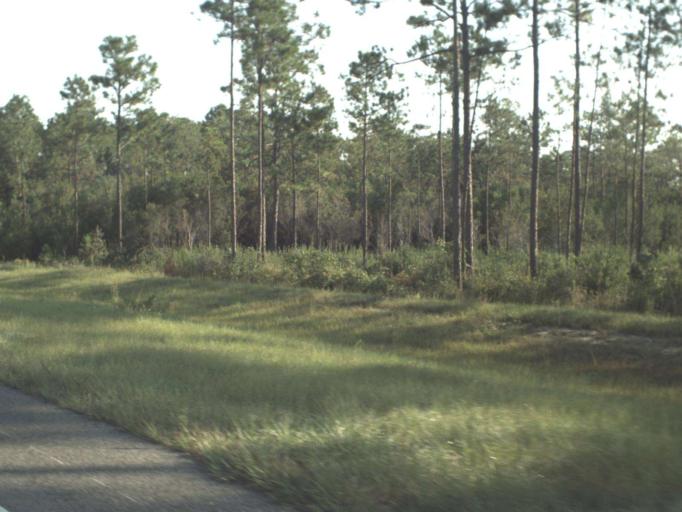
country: US
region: Florida
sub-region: Bay County
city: Laguna Beach
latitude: 30.4264
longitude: -85.8750
